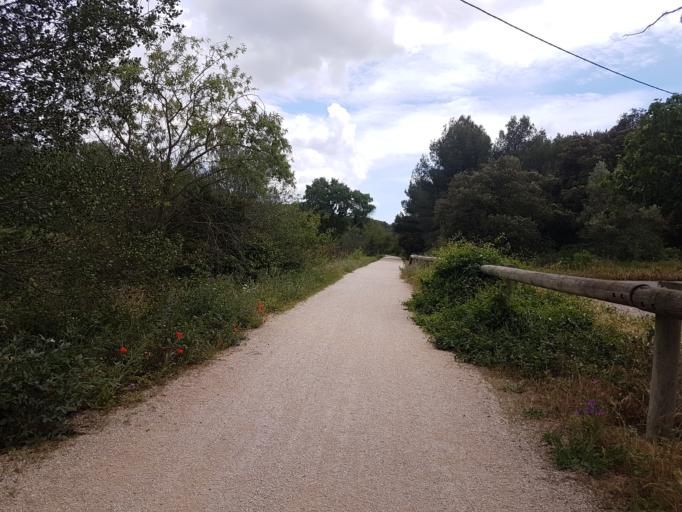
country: FR
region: Languedoc-Roussillon
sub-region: Departement du Gard
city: Vallabregues
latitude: 43.8293
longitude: 4.6199
